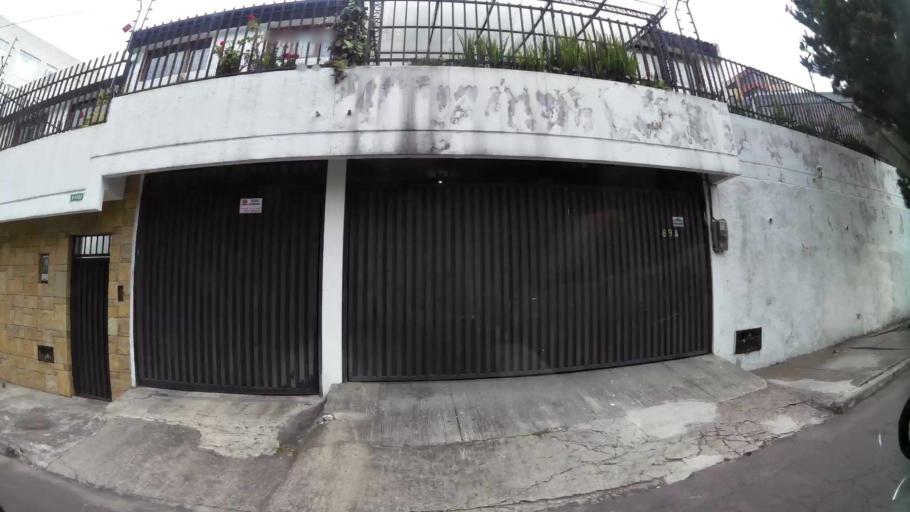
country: EC
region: Pichincha
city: Quito
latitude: -0.1654
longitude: -78.4943
